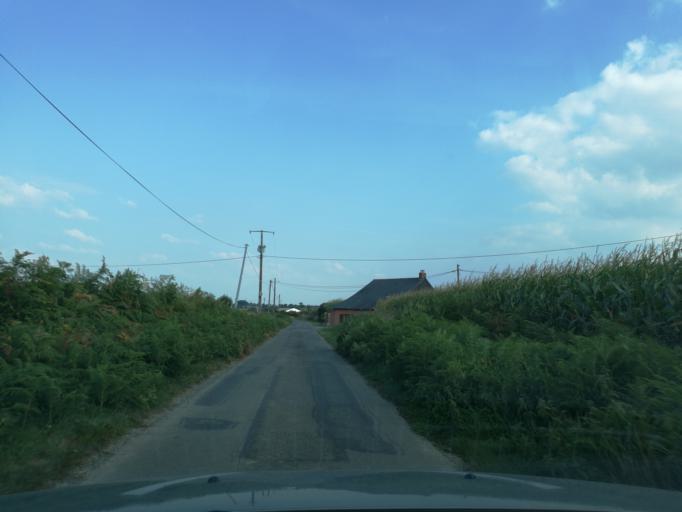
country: FR
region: Brittany
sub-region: Departement d'Ille-et-Vilaine
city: Bedee
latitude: 48.1892
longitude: -1.9937
